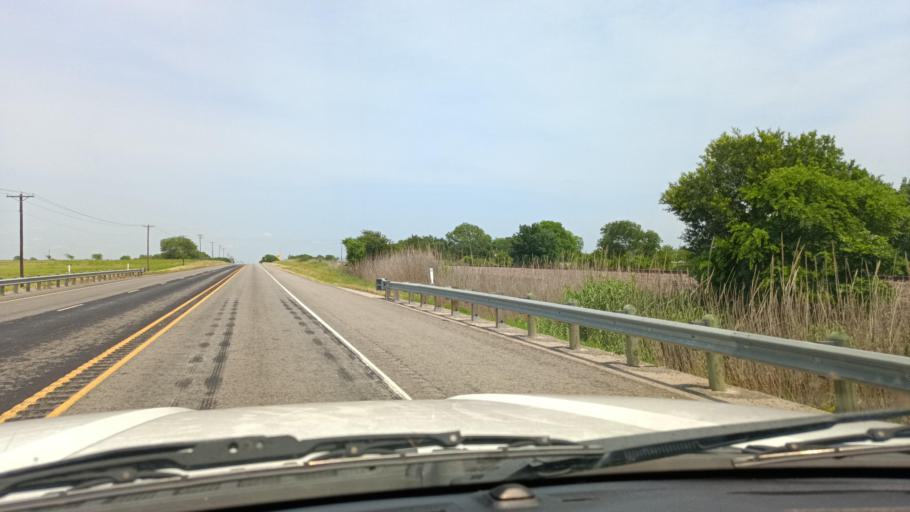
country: US
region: Texas
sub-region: Milam County
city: Cameron
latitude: 30.8488
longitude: -97.0561
